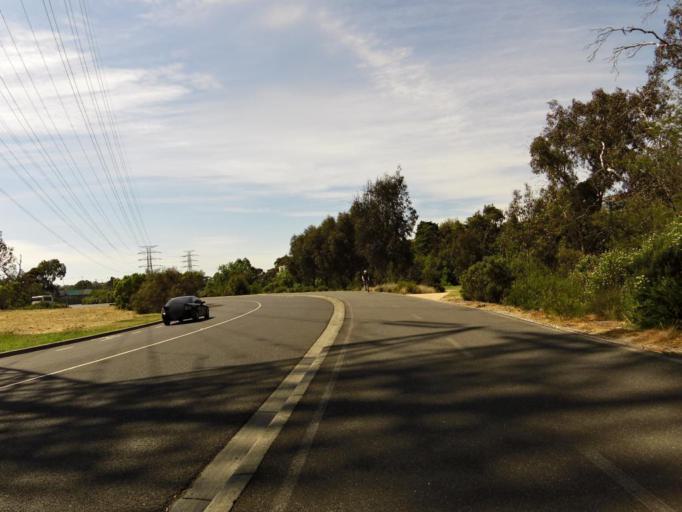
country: AU
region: Victoria
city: Toorak
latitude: -37.8315
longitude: 145.0162
